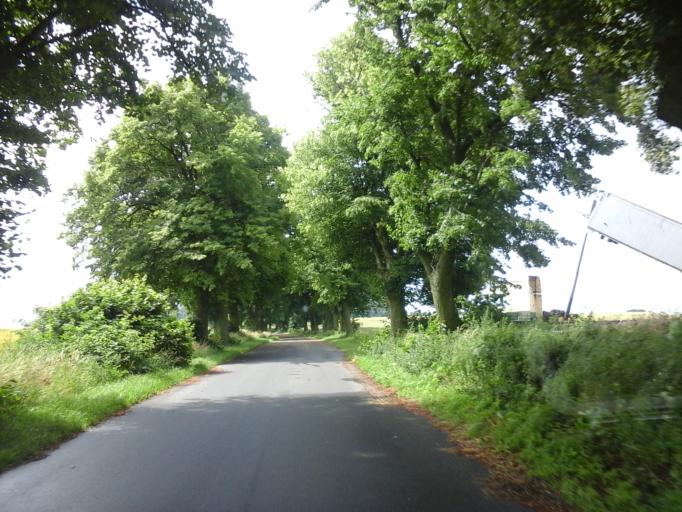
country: PL
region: West Pomeranian Voivodeship
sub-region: Powiat choszczenski
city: Krzecin
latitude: 53.0386
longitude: 15.4597
